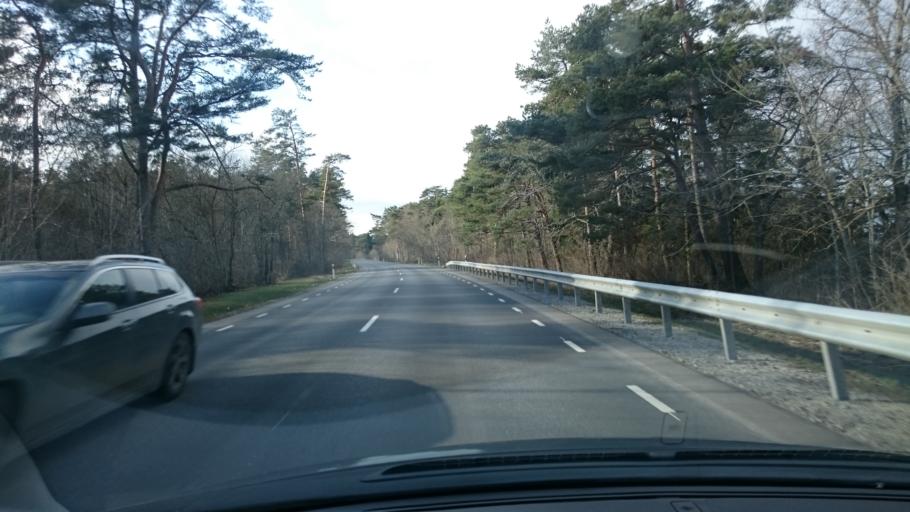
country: EE
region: Harju
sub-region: Keila linn
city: Keila
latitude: 59.3979
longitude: 24.2512
